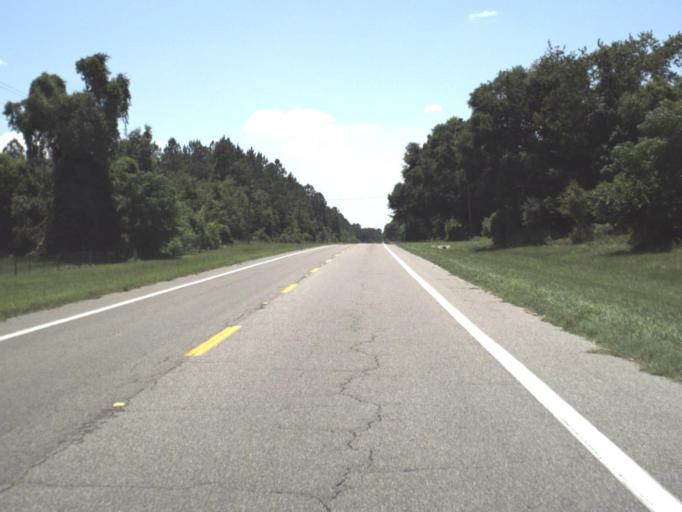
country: US
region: Florida
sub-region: Lafayette County
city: Mayo
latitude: 30.0531
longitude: -83.1329
